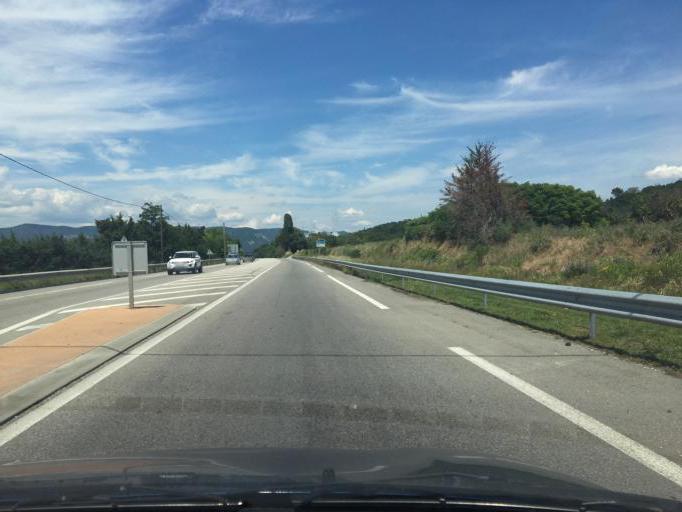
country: FR
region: Rhone-Alpes
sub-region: Departement de la Drome
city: Montelimar
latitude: 44.5828
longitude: 4.7527
